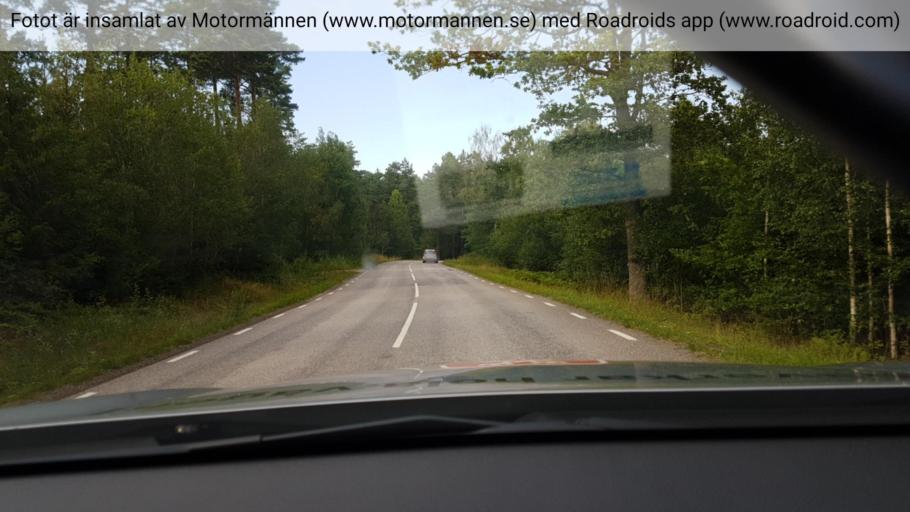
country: SE
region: Vaestra Goetaland
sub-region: Lidkopings Kommun
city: Lidkoping
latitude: 58.6236
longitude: 13.1298
